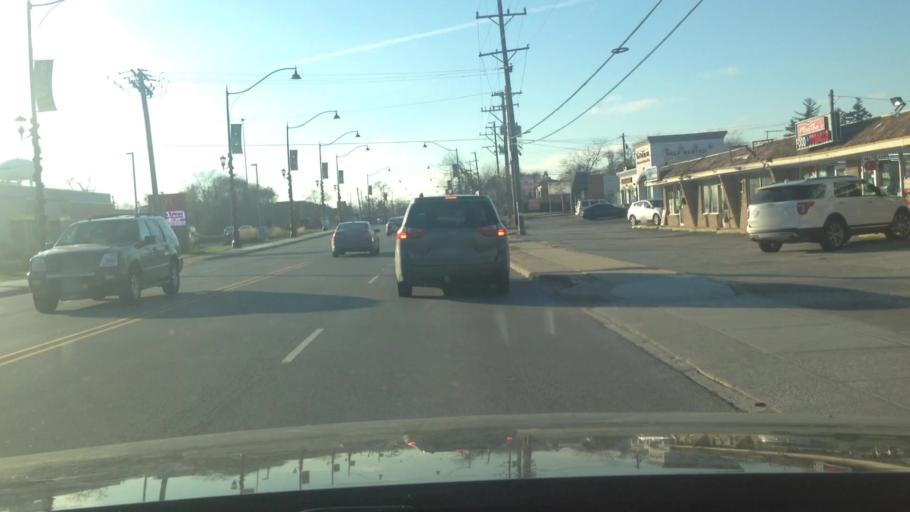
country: US
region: Illinois
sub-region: DuPage County
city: Bensenville
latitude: 41.9610
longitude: -87.9438
